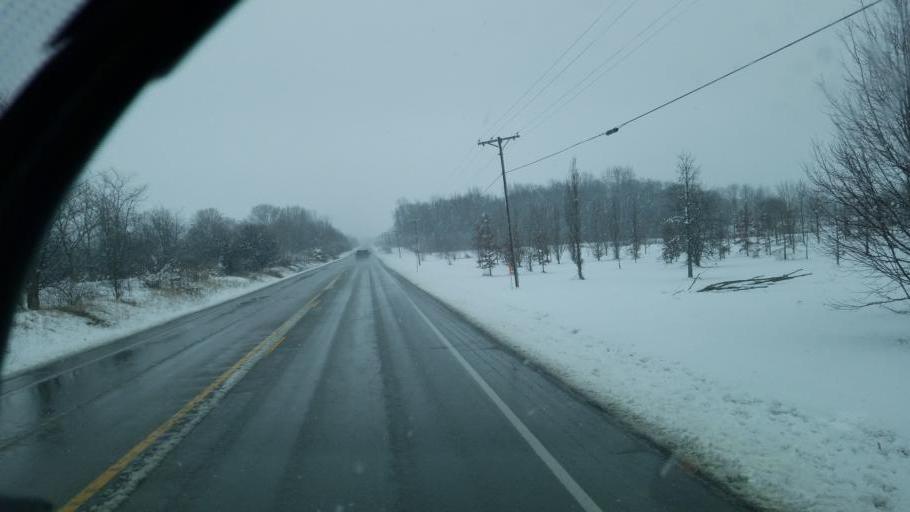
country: US
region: Indiana
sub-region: Delaware County
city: Muncie
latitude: 40.1367
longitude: -85.3353
